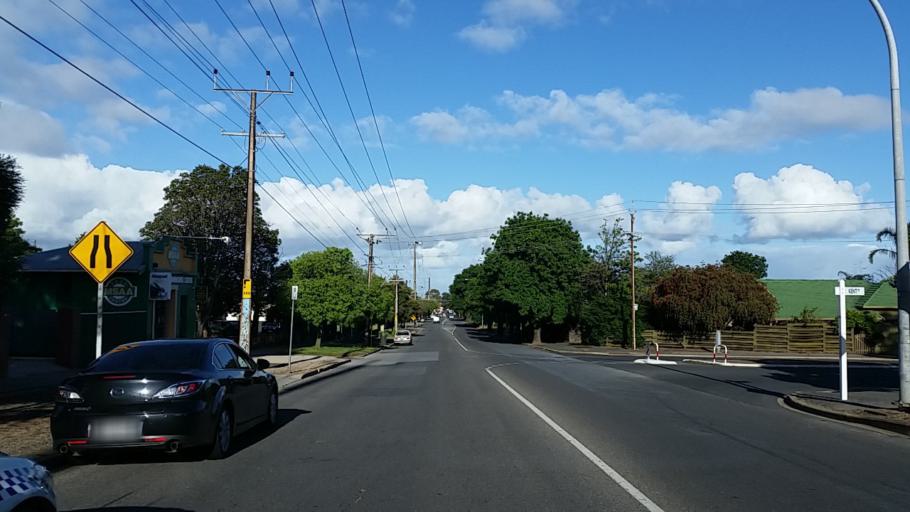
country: AU
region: South Australia
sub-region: Mitcham
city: Clapham
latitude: -34.9905
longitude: 138.5993
